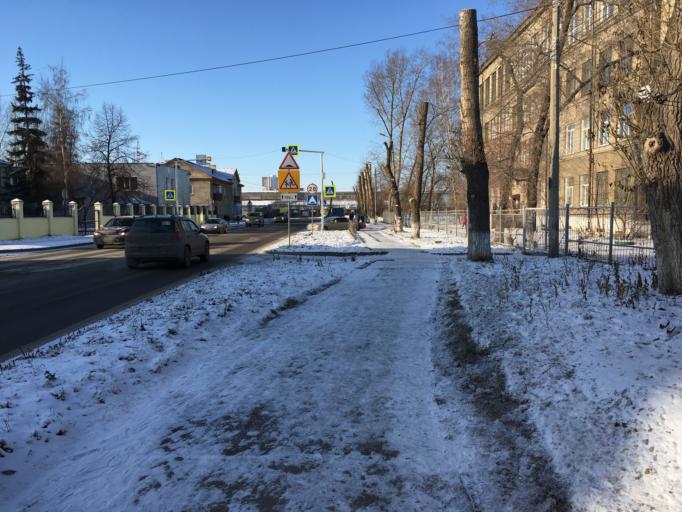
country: RU
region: Novosibirsk
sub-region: Novosibirskiy Rayon
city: Novosibirsk
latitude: 55.0529
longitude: 82.9618
